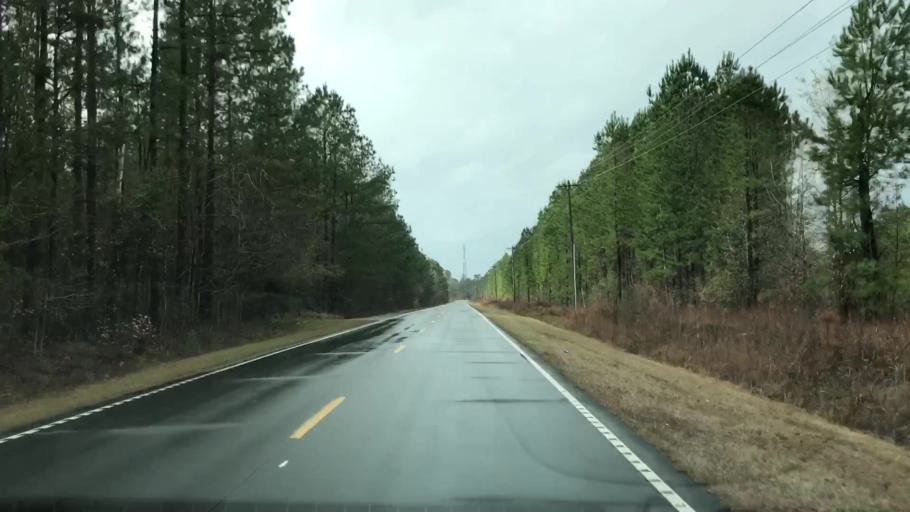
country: US
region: South Carolina
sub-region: Florence County
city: Johnsonville
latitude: 33.6762
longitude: -79.3437
